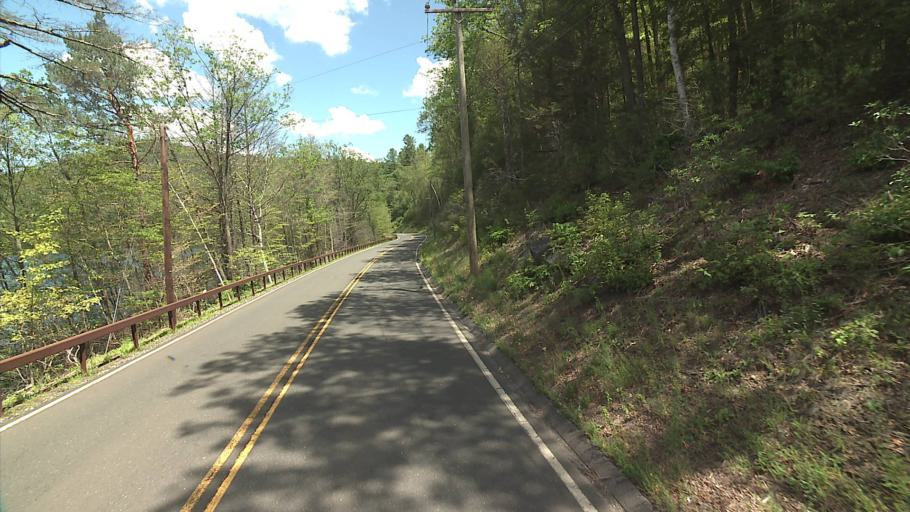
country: US
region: Connecticut
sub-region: Litchfield County
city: New Hartford Center
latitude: 41.8858
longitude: -72.9534
